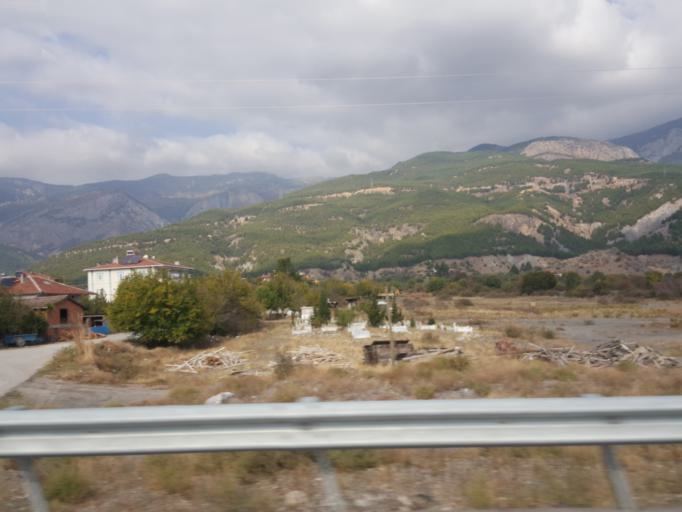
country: TR
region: Corum
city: Kargi
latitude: 41.1312
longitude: 34.4283
